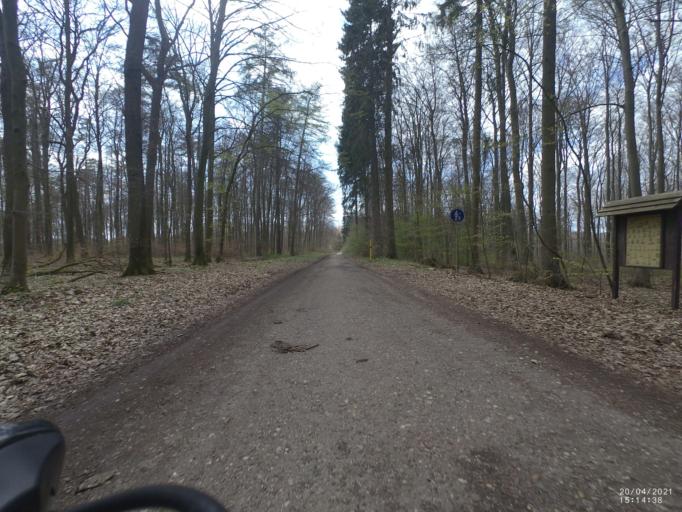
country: DE
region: Rheinland-Pfalz
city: Nauort
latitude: 50.4371
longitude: 7.6300
